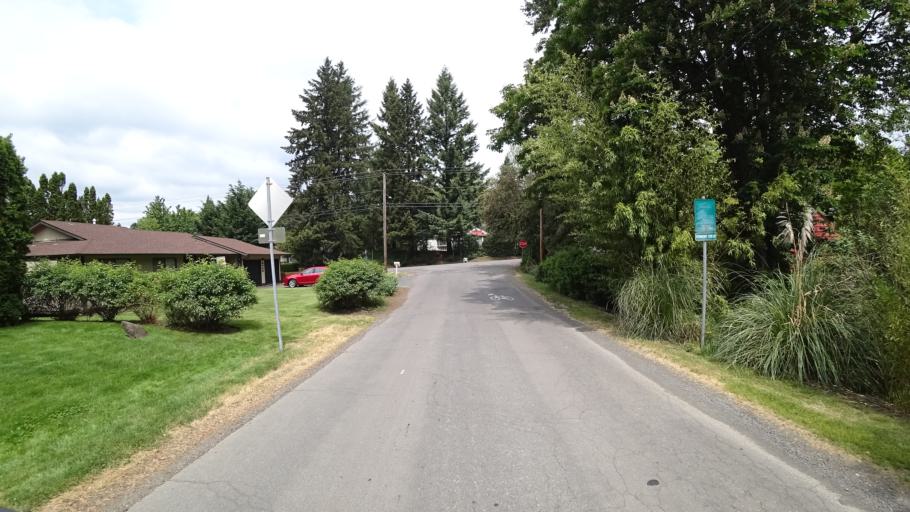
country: US
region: Oregon
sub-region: Washington County
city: Garden Home-Whitford
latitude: 45.4759
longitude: -122.7307
